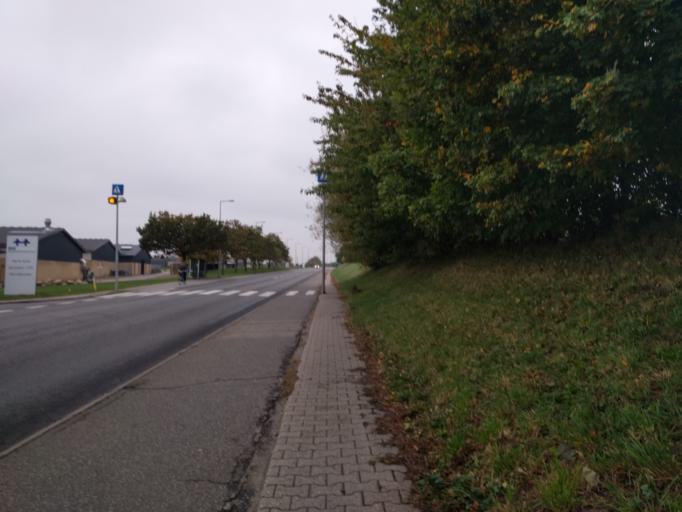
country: DK
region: South Denmark
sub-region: Fredericia Kommune
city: Snoghoj
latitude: 55.5381
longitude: 9.7129
